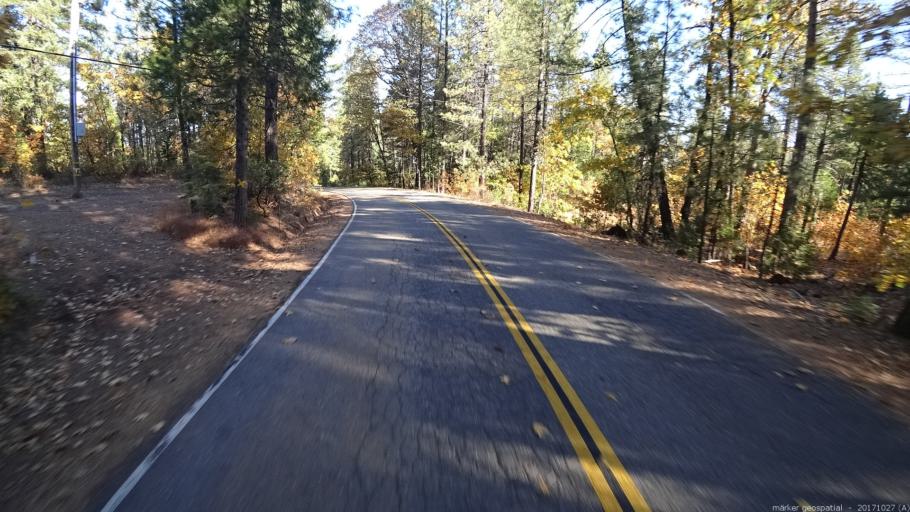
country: US
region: California
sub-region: Shasta County
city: Burney
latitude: 40.9963
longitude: -121.9199
